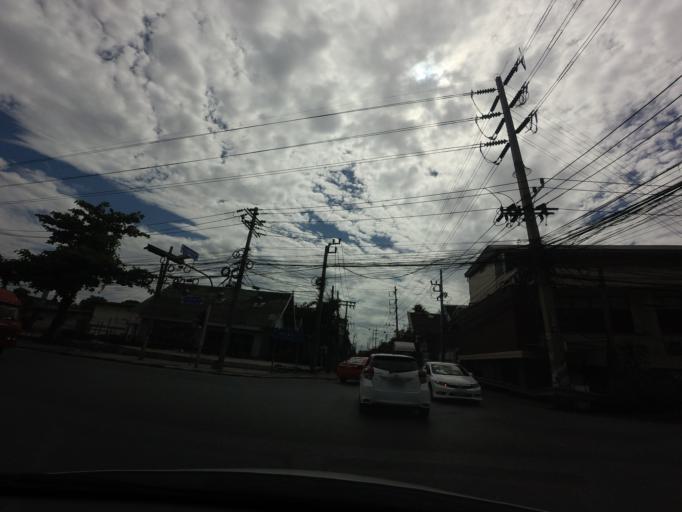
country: TH
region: Bangkok
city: Phra Khanong
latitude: 13.6761
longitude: 100.5912
